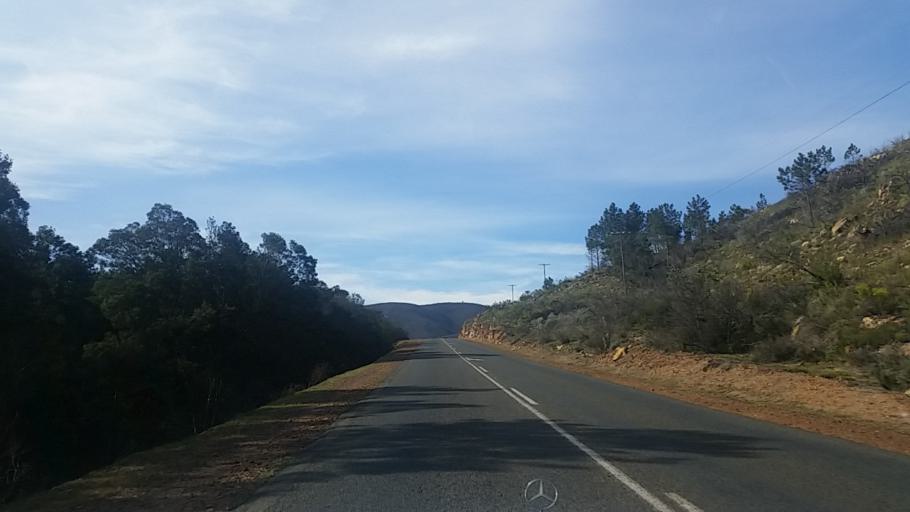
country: ZA
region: Western Cape
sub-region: Eden District Municipality
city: George
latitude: -33.8313
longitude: 22.3489
